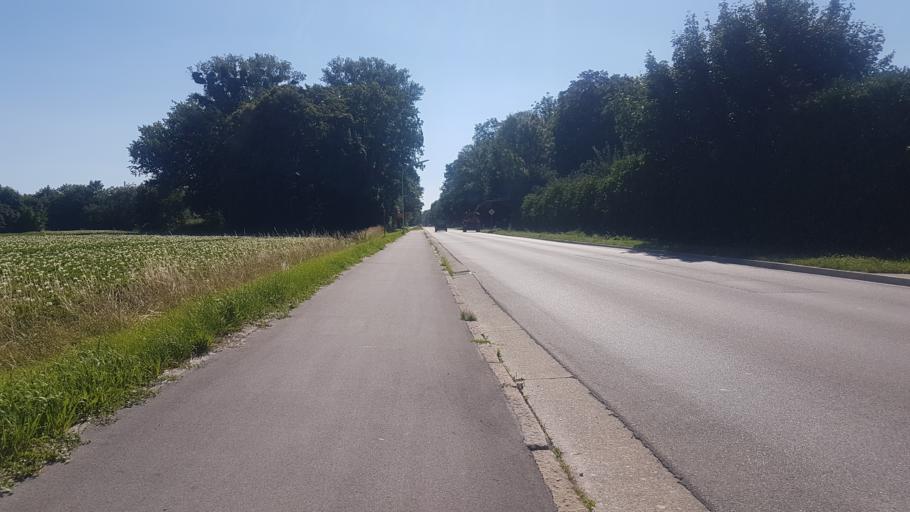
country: DE
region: Bavaria
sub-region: Upper Bavaria
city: Bergheim
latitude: 48.7377
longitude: 11.2322
